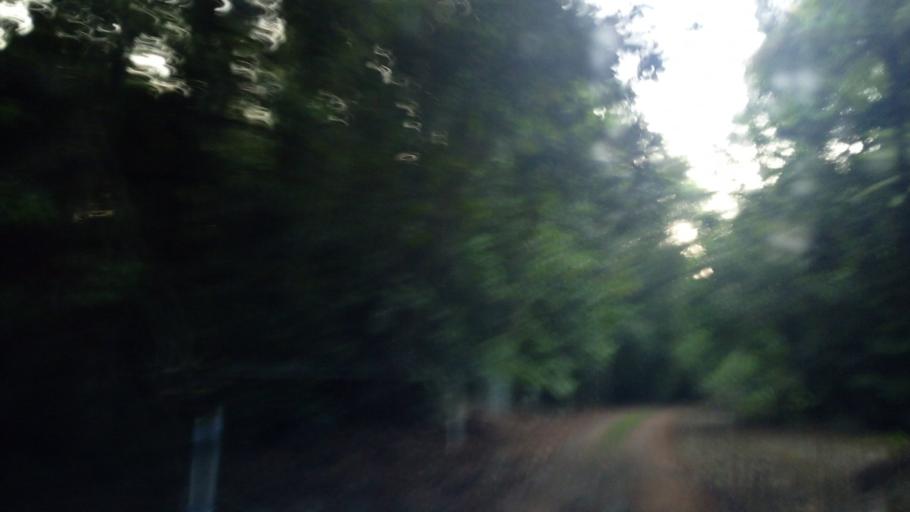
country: AU
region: Queensland
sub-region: Tablelands
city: Atherton
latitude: -17.3772
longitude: 145.7592
